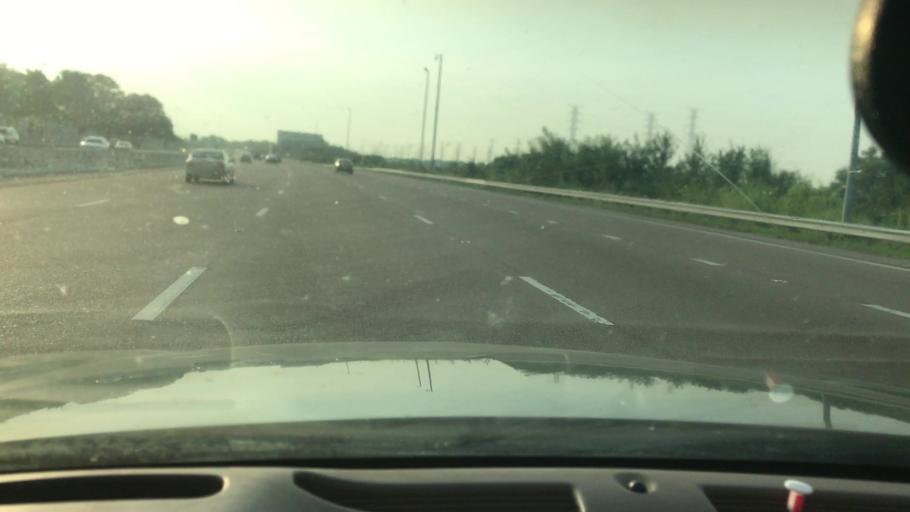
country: US
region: Tennessee
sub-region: Shelby County
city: Germantown
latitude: 35.0780
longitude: -89.9179
